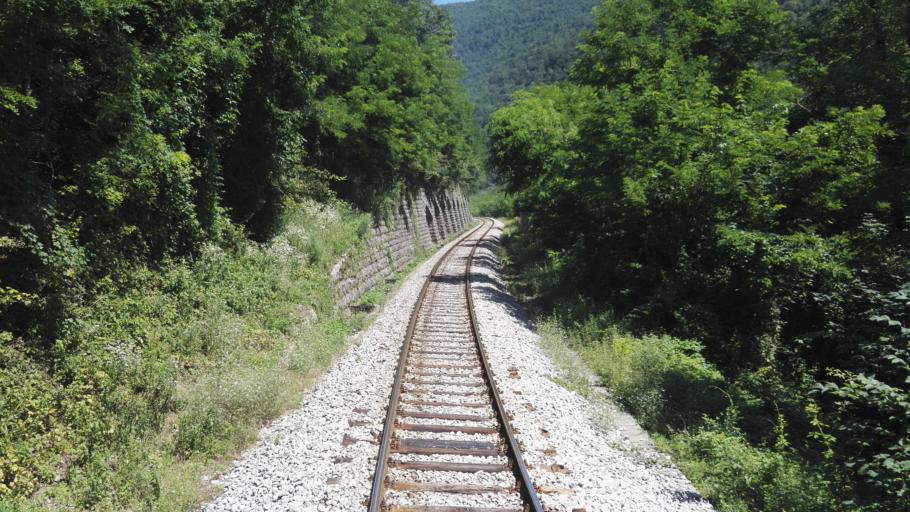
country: SI
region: Kanal
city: Deskle
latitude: 46.0192
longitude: 13.6057
